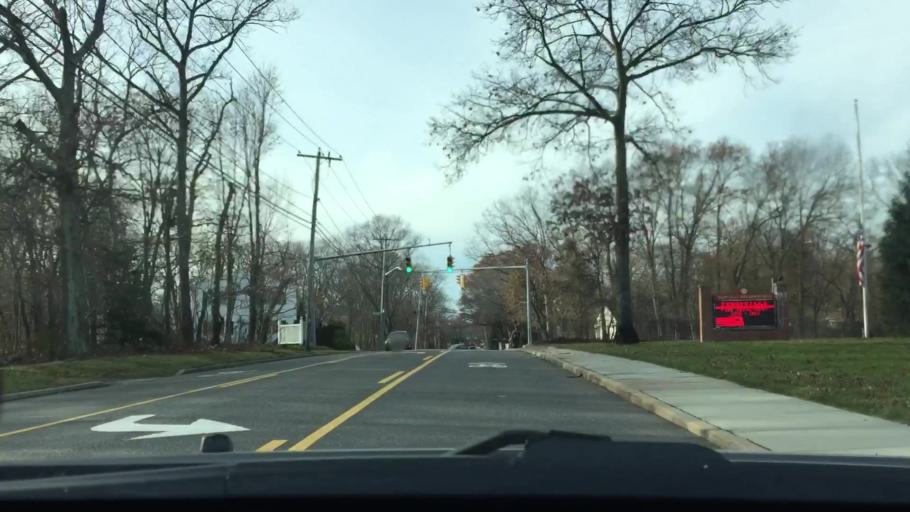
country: US
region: New York
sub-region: Suffolk County
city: Port Jefferson Station
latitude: 40.9198
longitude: -73.0266
